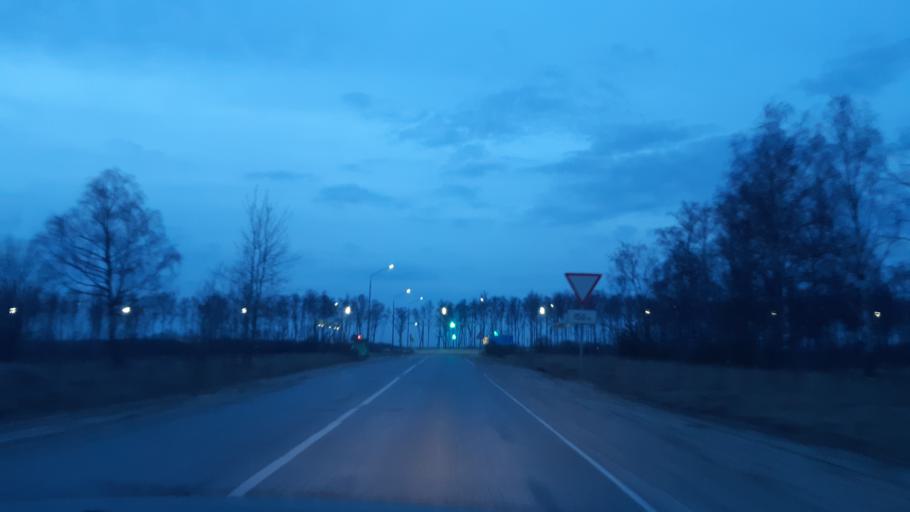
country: RU
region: Vladimir
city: Luknovo
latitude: 56.2366
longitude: 42.0342
